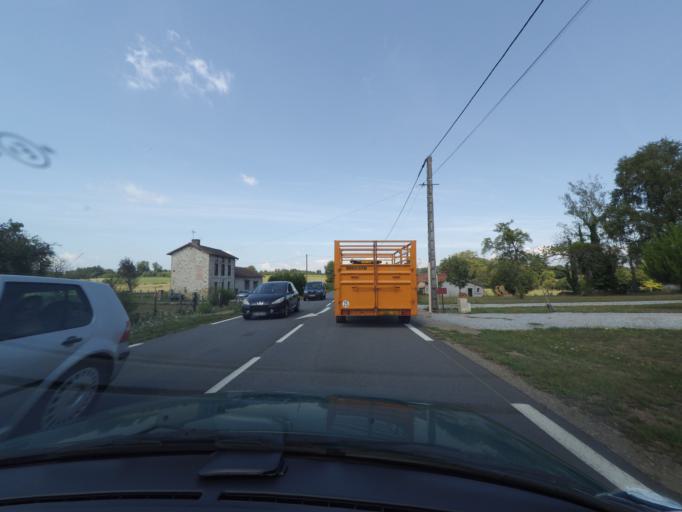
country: FR
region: Limousin
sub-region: Departement de la Haute-Vienne
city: Saint-Paul
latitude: 45.7903
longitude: 1.4622
